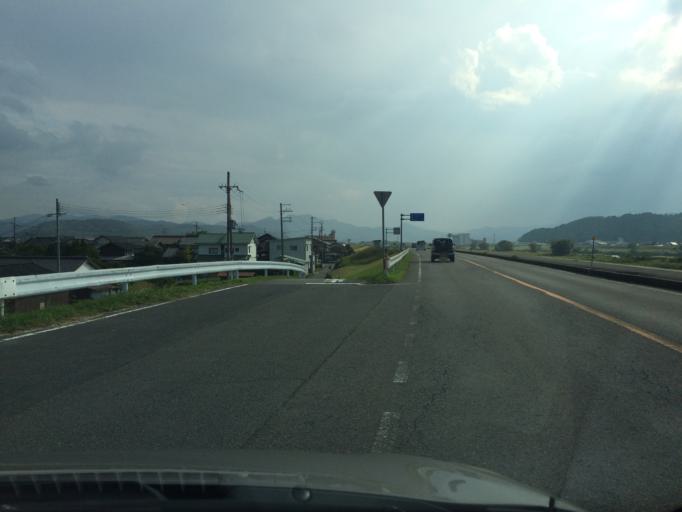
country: JP
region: Hyogo
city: Toyooka
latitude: 35.5255
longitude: 134.8269
